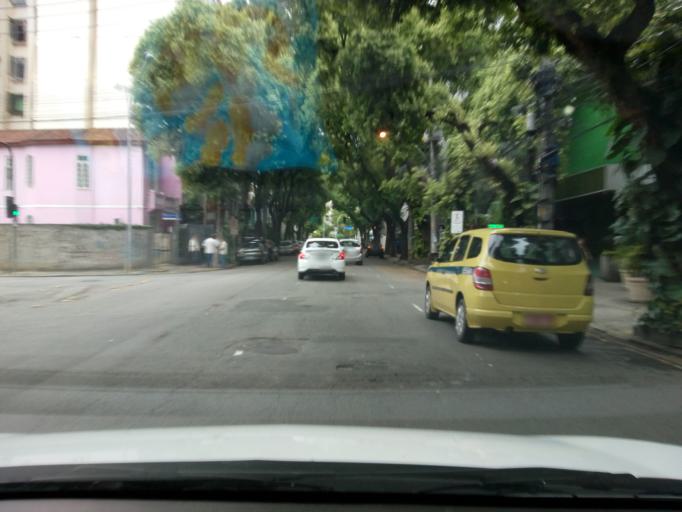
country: BR
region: Rio de Janeiro
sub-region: Rio De Janeiro
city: Rio de Janeiro
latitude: -22.9192
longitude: -43.2257
